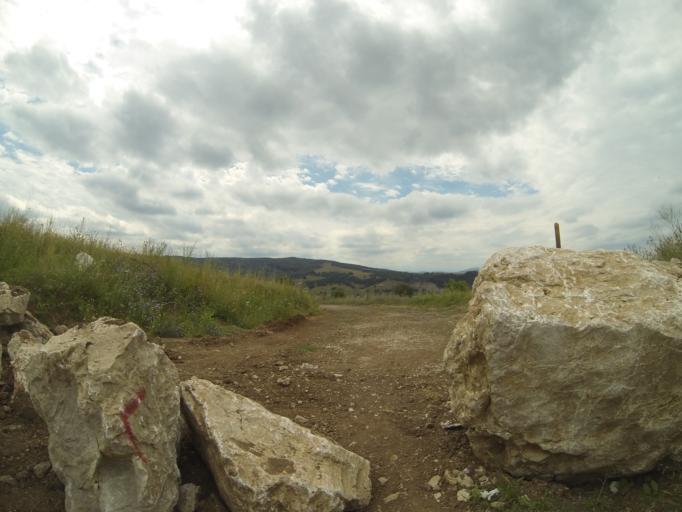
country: RO
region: Brasov
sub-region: Comuna Hoghiz
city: Hoghiz
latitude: 46.0307
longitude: 25.4172
